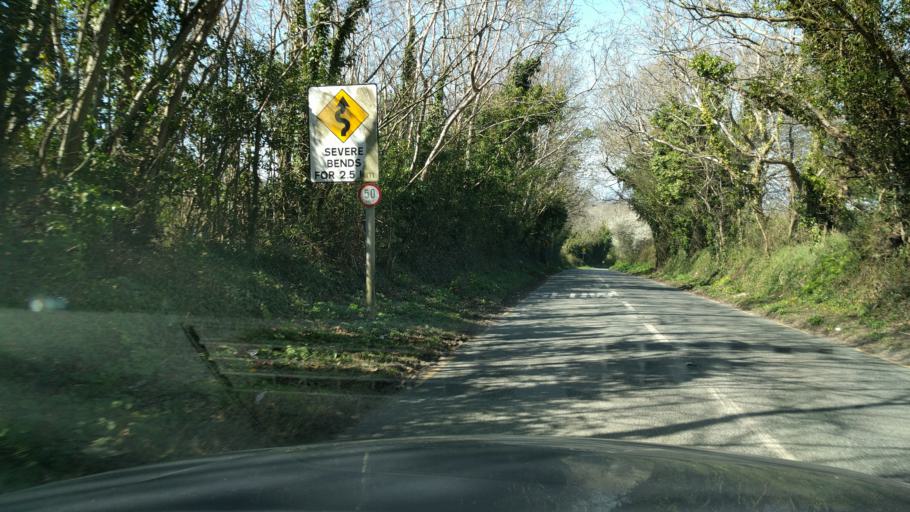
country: IE
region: Leinster
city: Ballyboden
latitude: 53.2619
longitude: -6.3206
